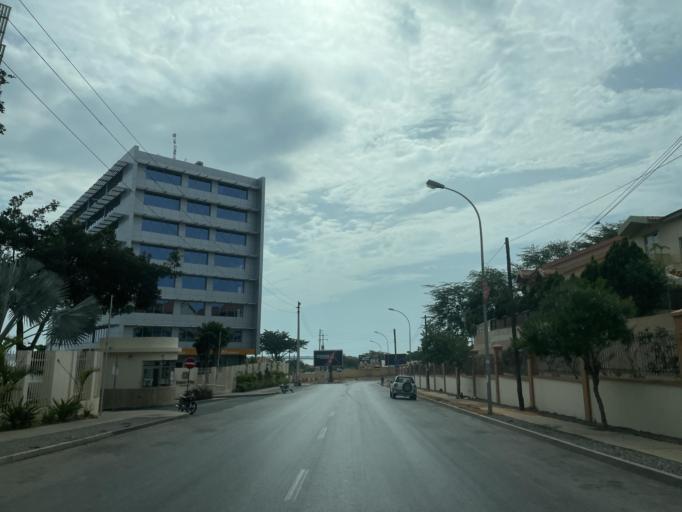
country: AO
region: Luanda
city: Luanda
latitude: -8.9218
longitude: 13.1715
